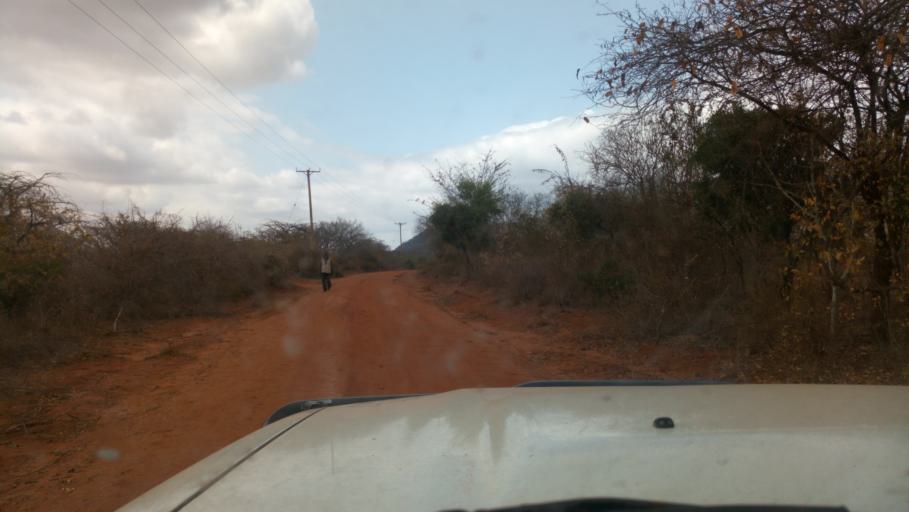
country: KE
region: Kitui
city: Kitui
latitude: -1.8439
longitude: 38.3396
